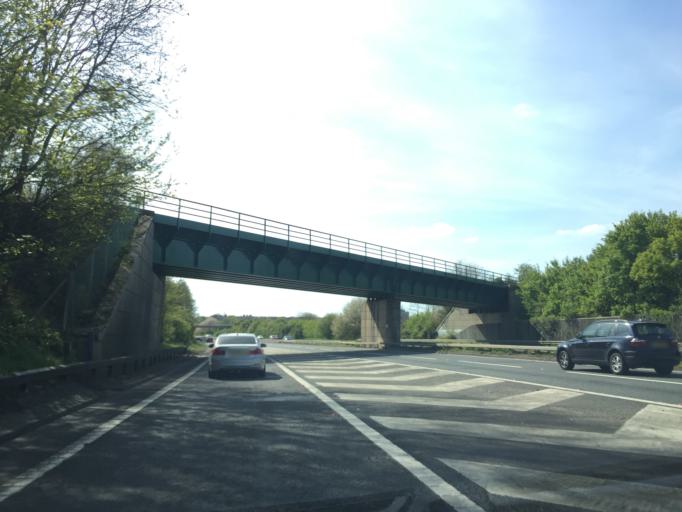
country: GB
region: England
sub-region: Kent
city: Swanley
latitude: 51.3895
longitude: 0.1861
